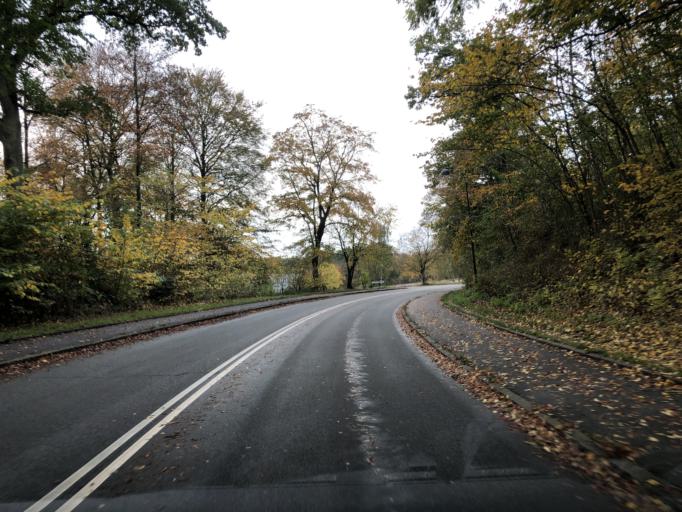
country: DK
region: Capital Region
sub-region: Lyngby-Tarbaek Kommune
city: Kongens Lyngby
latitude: 55.8012
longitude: 12.5019
